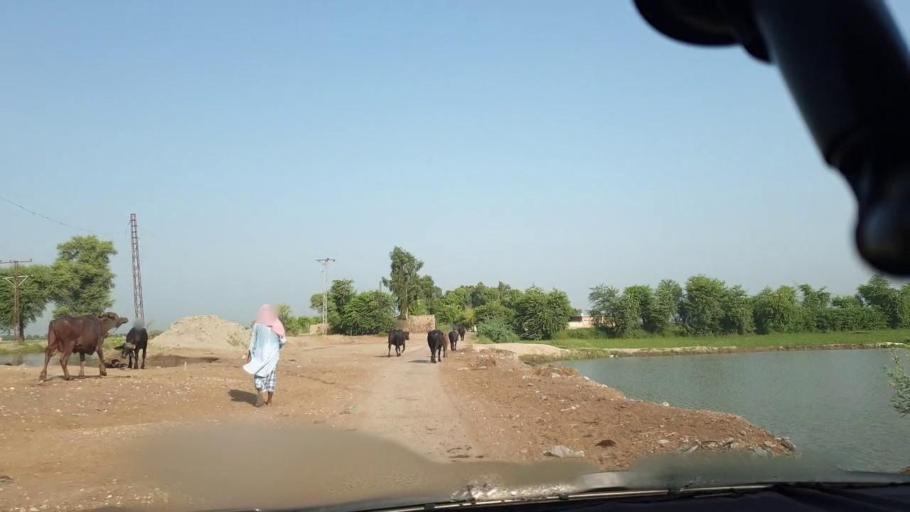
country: PK
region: Sindh
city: Larkana
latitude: 27.6179
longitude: 68.2172
